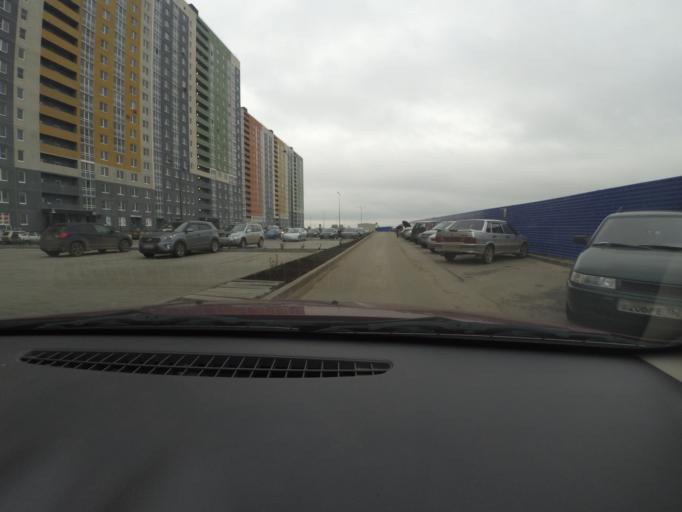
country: RU
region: Nizjnij Novgorod
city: Afonino
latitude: 56.2487
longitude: 44.0426
